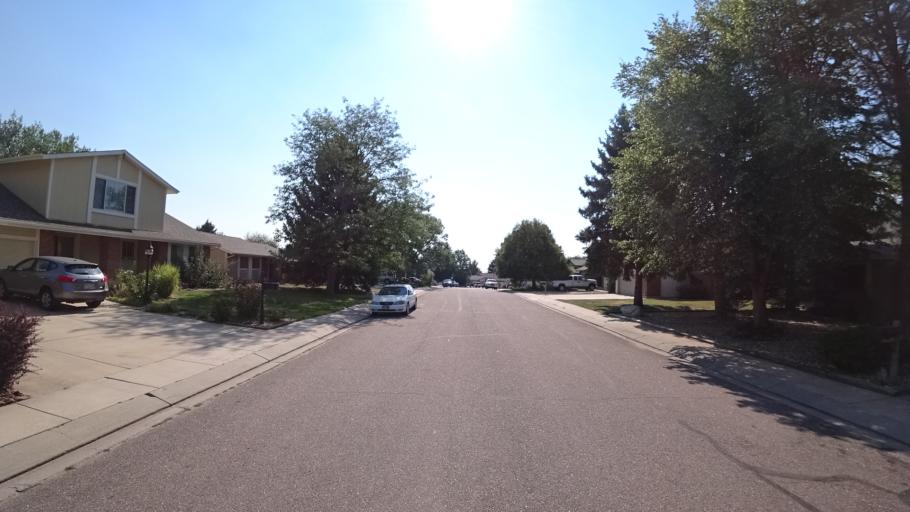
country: US
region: Colorado
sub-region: El Paso County
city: Stratmoor
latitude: 38.7883
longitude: -104.8154
